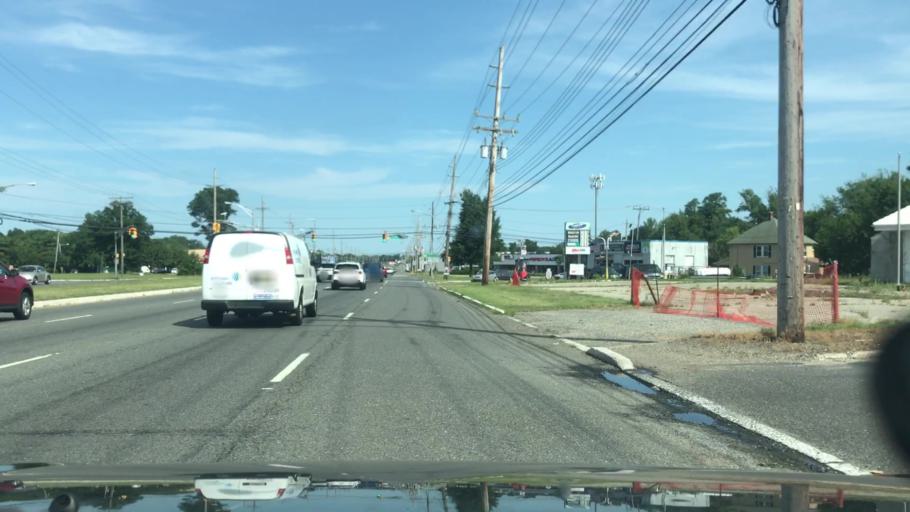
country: US
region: New Jersey
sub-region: Ocean County
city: Toms River
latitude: 39.9608
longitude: -74.1784
